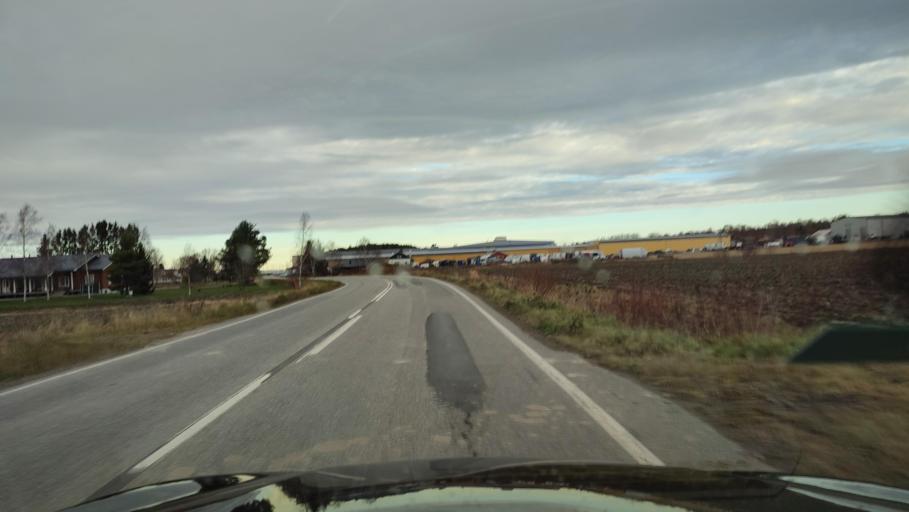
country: FI
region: Ostrobothnia
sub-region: Sydosterbotten
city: Naerpes
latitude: 62.4382
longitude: 21.3519
